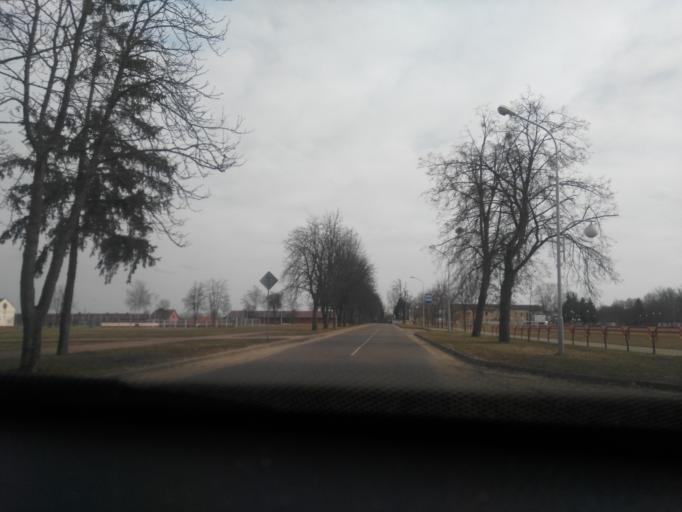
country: BY
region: Mogilev
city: Babruysk
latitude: 53.1413
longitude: 29.2437
